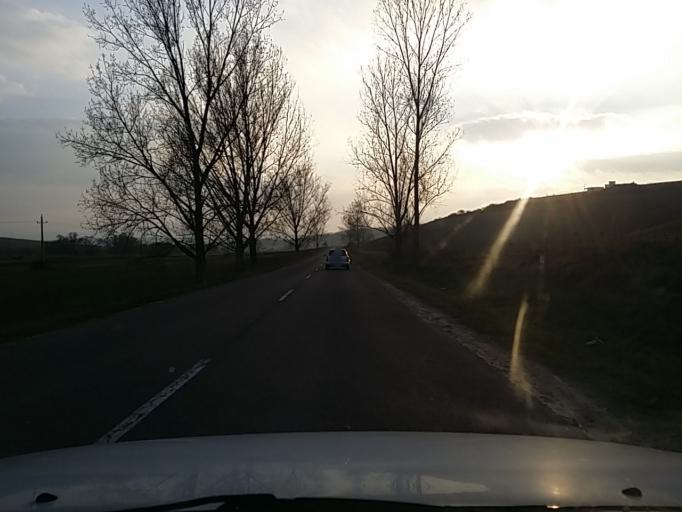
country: HU
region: Heves
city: Tarnalelesz
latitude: 48.0467
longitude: 20.1473
